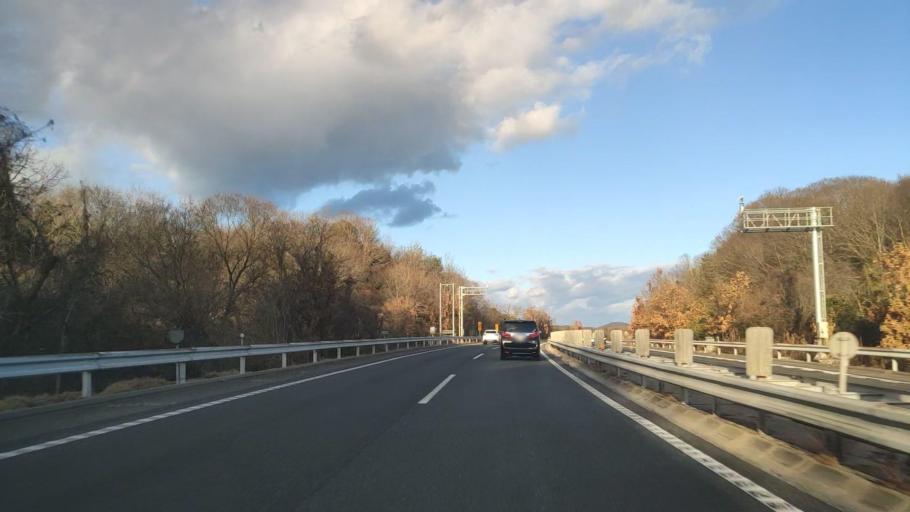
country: JP
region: Hyogo
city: Aioi
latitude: 34.8030
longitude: 134.4378
